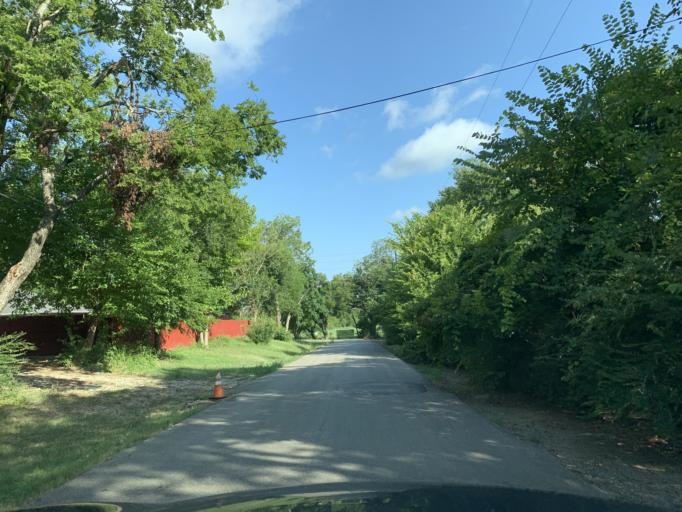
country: US
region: Texas
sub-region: Dallas County
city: Hutchins
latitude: 32.6764
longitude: -96.7820
